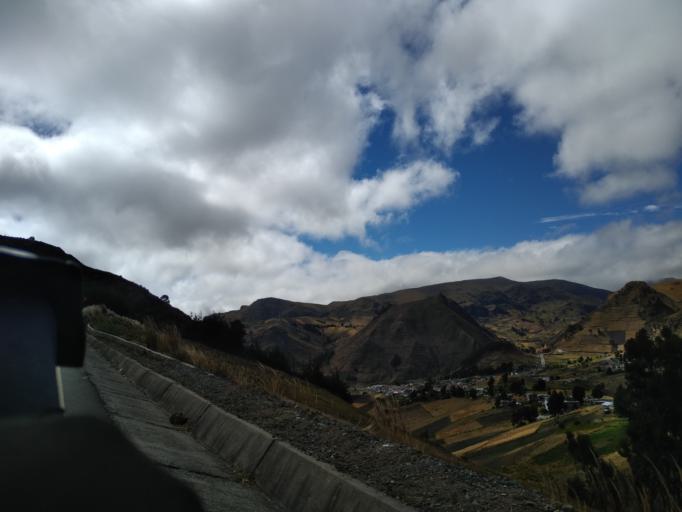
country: EC
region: Cotopaxi
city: Pujili
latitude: -0.9562
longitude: -78.9120
